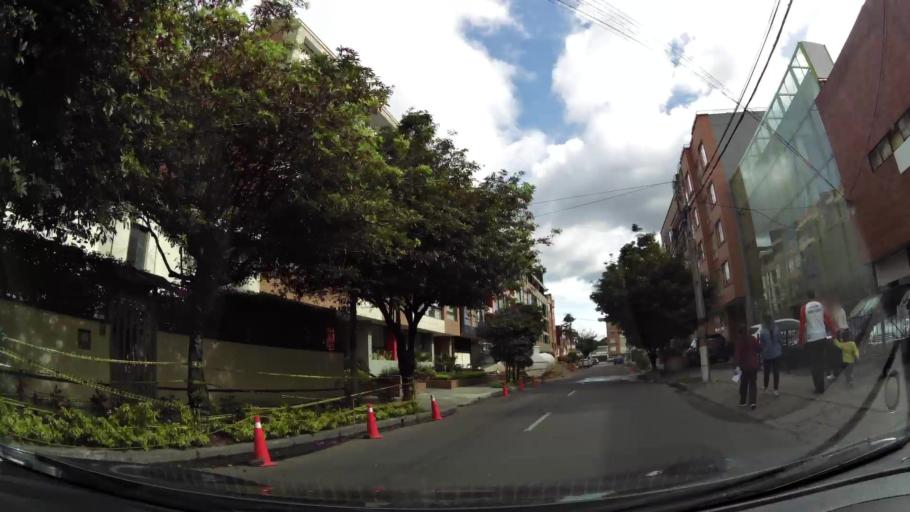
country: CO
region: Bogota D.C.
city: Barrio San Luis
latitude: 4.6914
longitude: -74.0619
